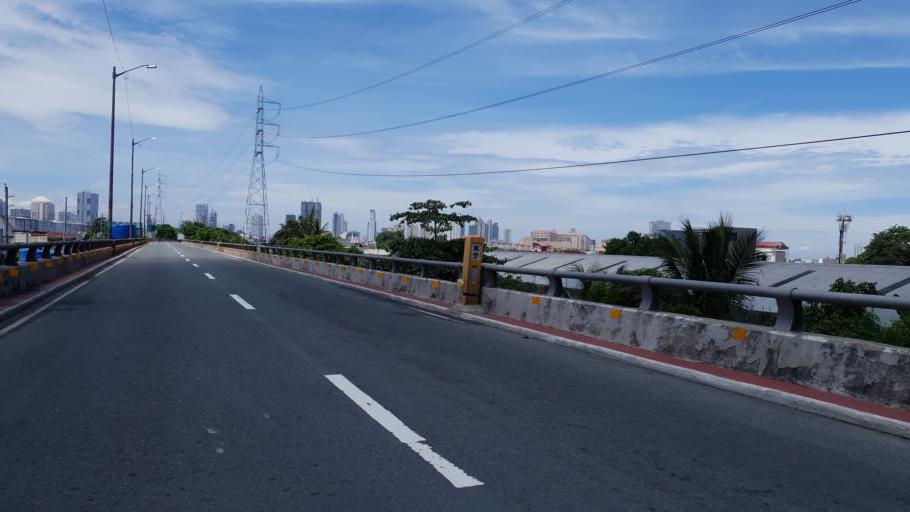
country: PH
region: Metro Manila
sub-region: San Juan
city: San Juan
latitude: 14.5900
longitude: 121.0087
